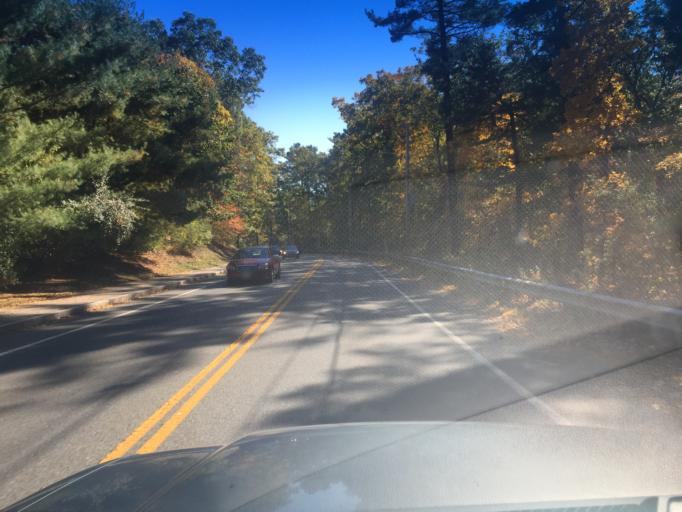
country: US
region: Massachusetts
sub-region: Middlesex County
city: Hudson
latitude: 42.3782
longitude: -71.5565
